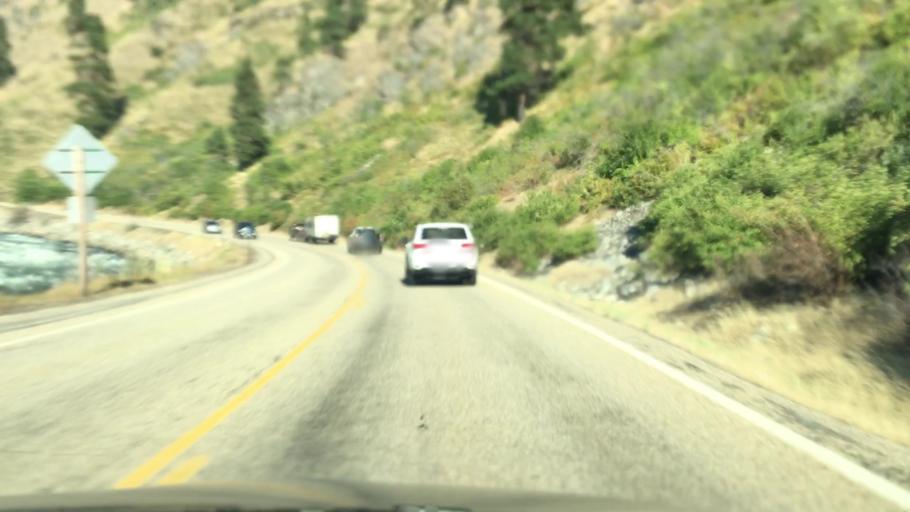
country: US
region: Idaho
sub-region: Boise County
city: Idaho City
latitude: 44.0890
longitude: -116.1085
